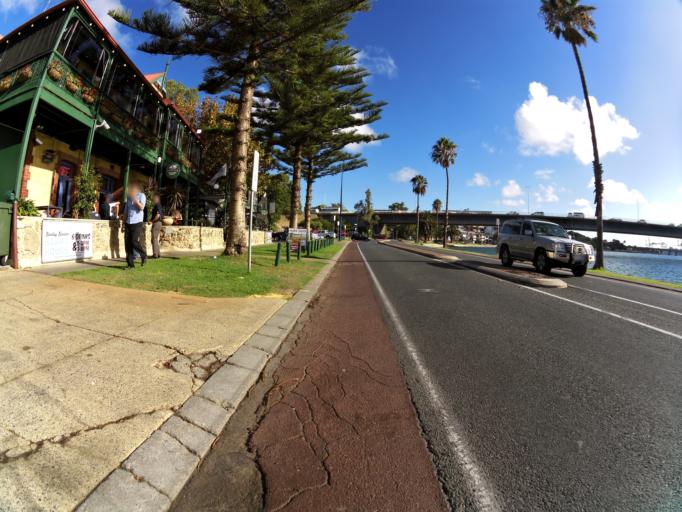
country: AU
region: Western Australia
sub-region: East Fremantle
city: East Fremantle
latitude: -32.0392
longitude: 115.7613
